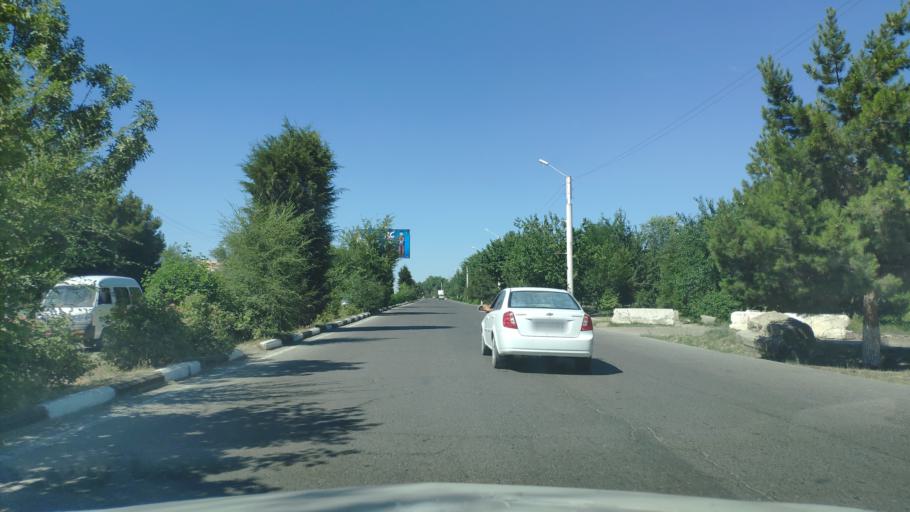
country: UZ
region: Bukhara
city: Bukhara
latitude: 39.7944
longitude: 64.4211
